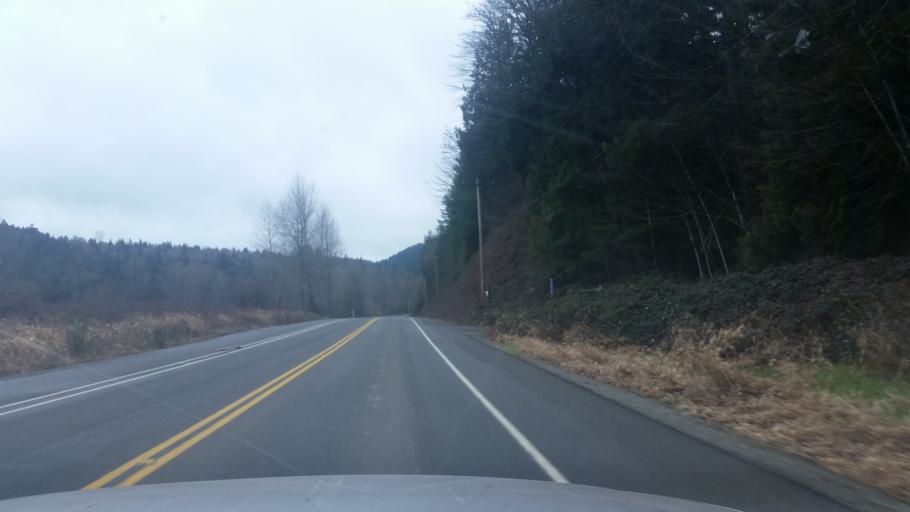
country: US
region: Washington
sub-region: King County
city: Fall City
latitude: 47.5328
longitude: -121.9511
